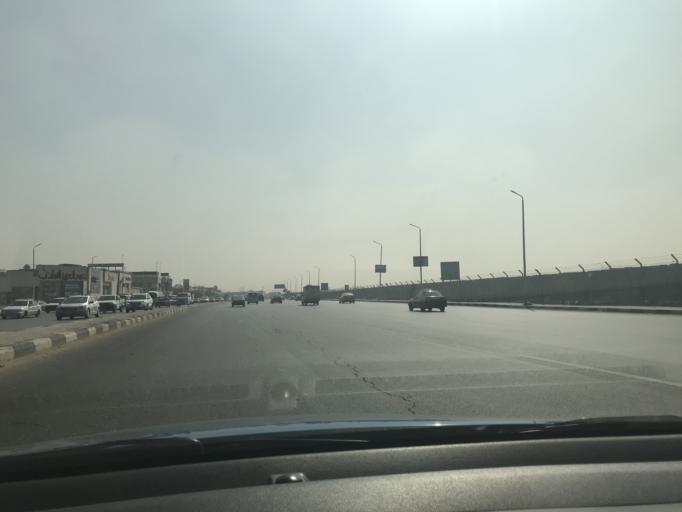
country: EG
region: Muhafazat al Qalyubiyah
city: Al Khankah
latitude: 30.1369
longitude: 31.3932
